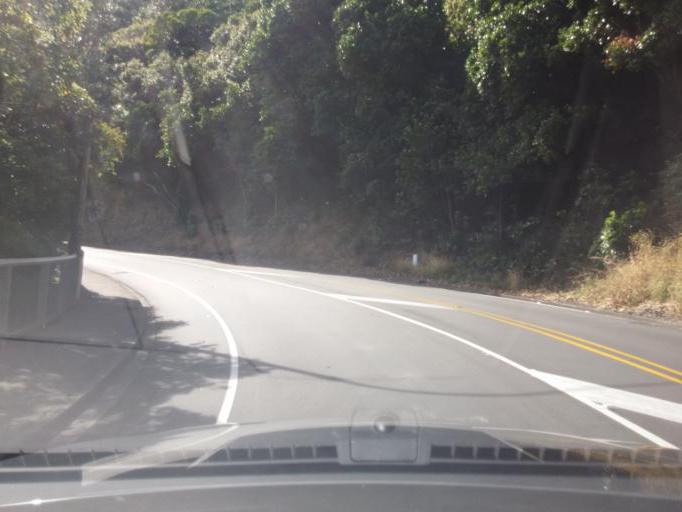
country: NZ
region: Wellington
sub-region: Wellington City
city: Kelburn
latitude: -41.2569
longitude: 174.7794
